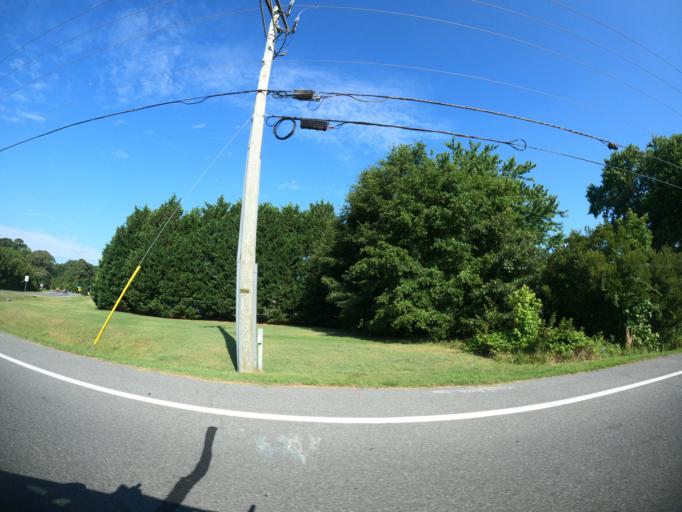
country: US
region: Delaware
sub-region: Sussex County
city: Ocean View
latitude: 38.5257
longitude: -75.0941
